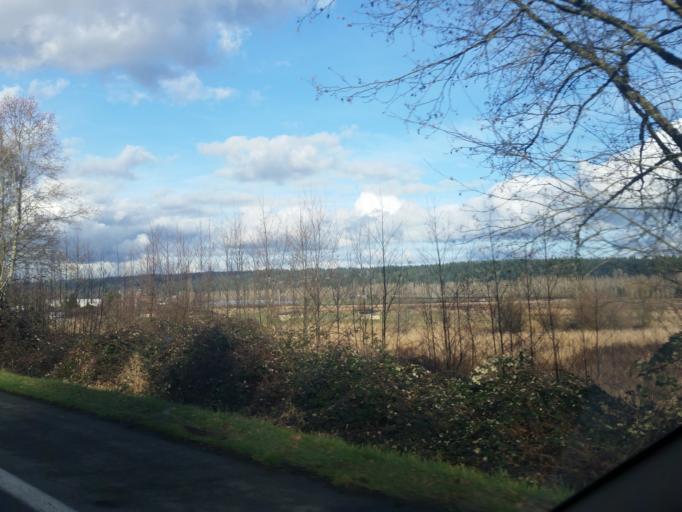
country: US
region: Washington
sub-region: King County
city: Kingsgate
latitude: 47.7078
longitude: -122.1539
